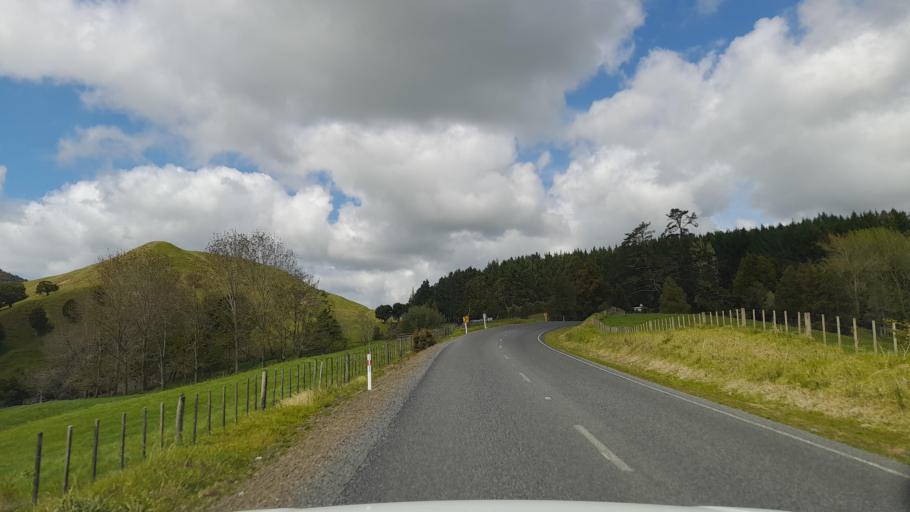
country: NZ
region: Northland
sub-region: Whangarei
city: Maungatapere
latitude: -35.6402
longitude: 174.1167
